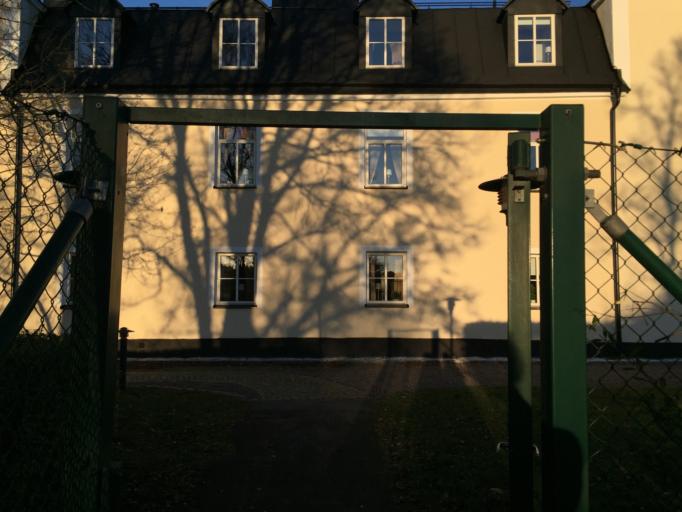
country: SE
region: OEstergoetland
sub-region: Soderkopings Kommun
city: Soederkoeping
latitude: 58.4785
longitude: 16.3307
